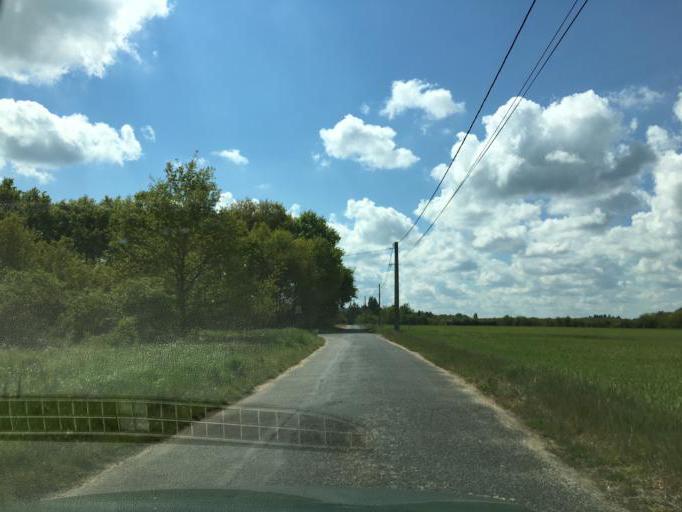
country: FR
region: Centre
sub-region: Departement du Loiret
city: Saint-Pryve-Saint-Mesmin
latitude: 47.8665
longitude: 1.8587
